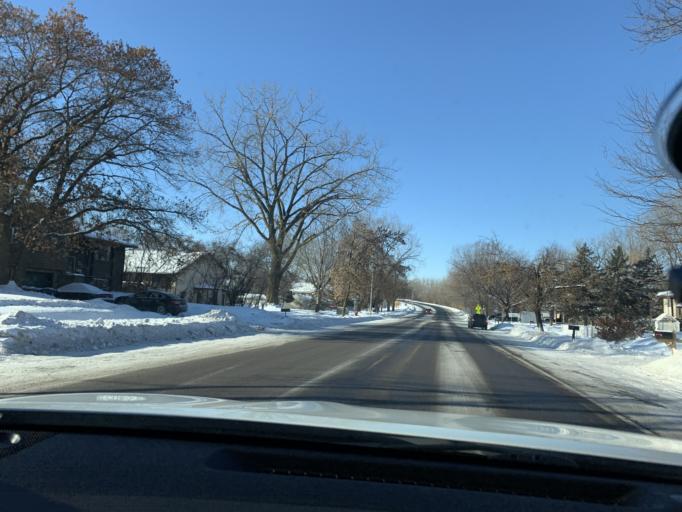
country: US
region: Minnesota
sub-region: Anoka County
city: Coon Rapids
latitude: 45.1638
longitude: -93.2807
